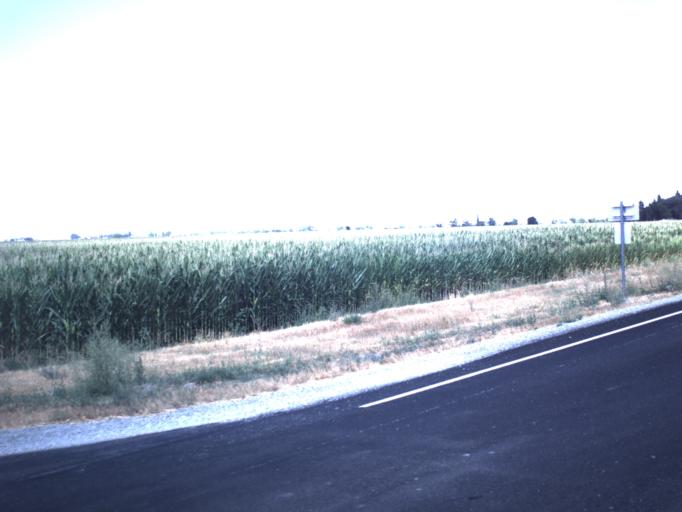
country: US
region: Utah
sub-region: Box Elder County
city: Honeyville
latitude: 41.6255
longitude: -112.1268
